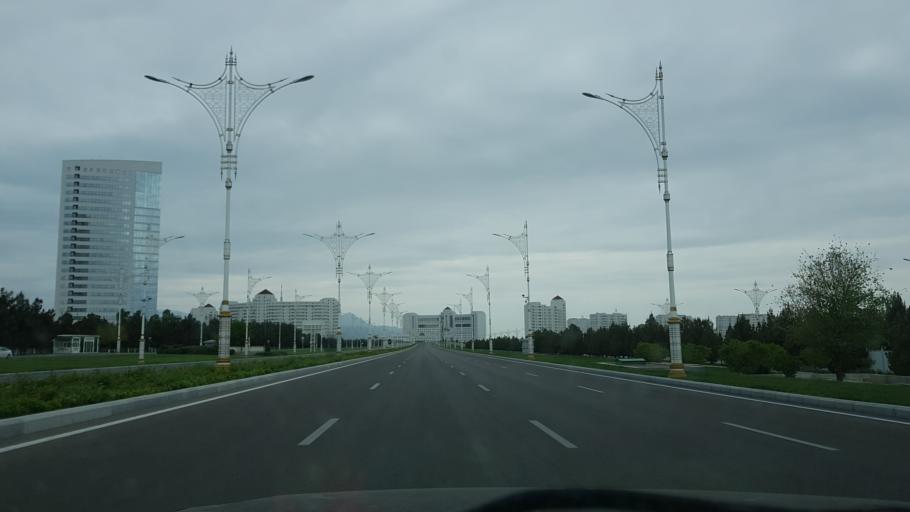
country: TM
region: Ahal
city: Ashgabat
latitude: 37.8904
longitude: 58.3469
